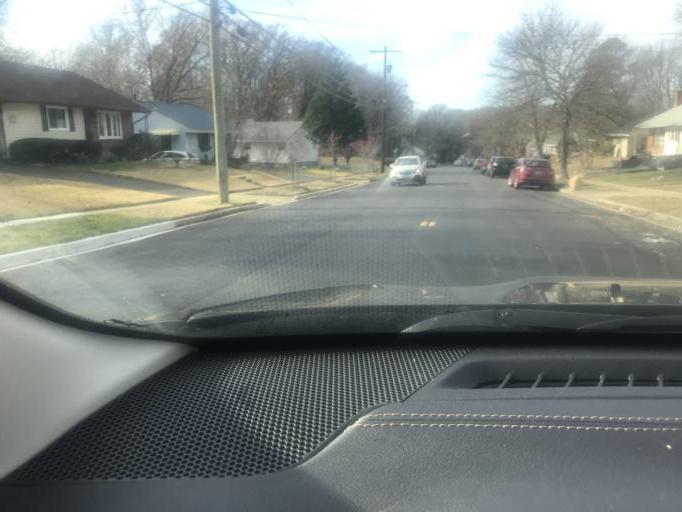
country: US
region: Maryland
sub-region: Prince George's County
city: Oxon Hill
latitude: 38.8086
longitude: -76.9862
